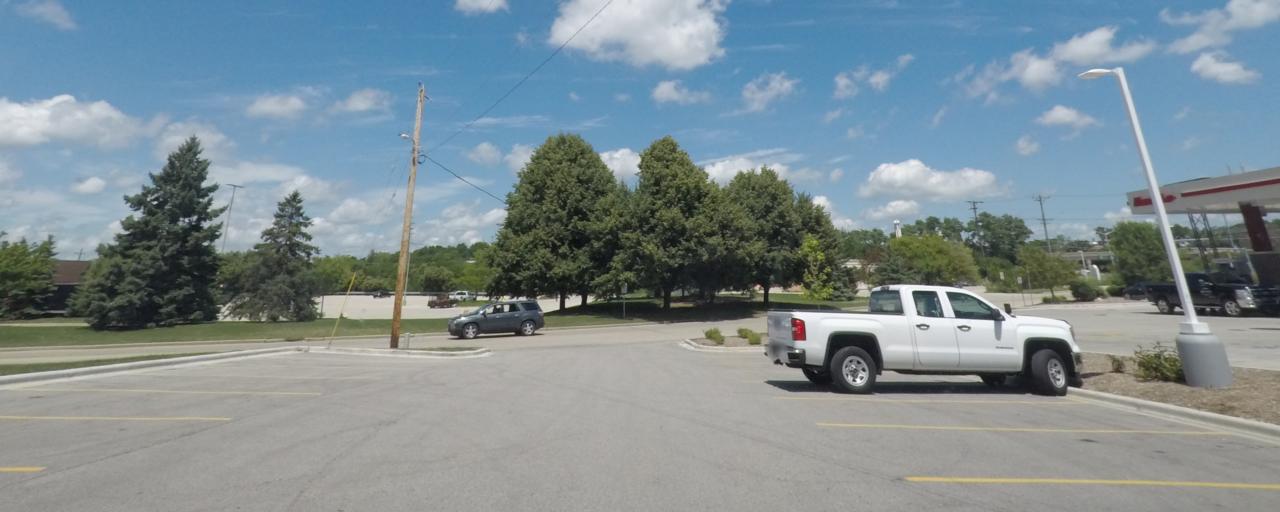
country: US
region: Wisconsin
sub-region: Waukesha County
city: Delafield
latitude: 43.0495
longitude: -88.3751
